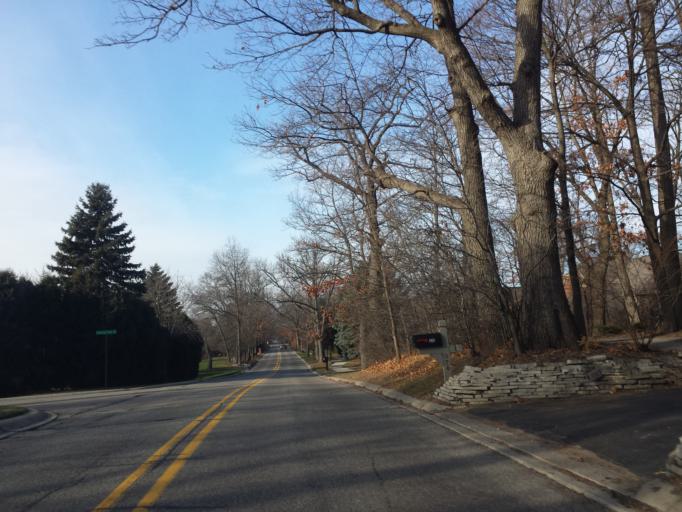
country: US
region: Michigan
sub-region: Oakland County
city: Bloomfield Hills
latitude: 42.5961
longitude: -83.2728
